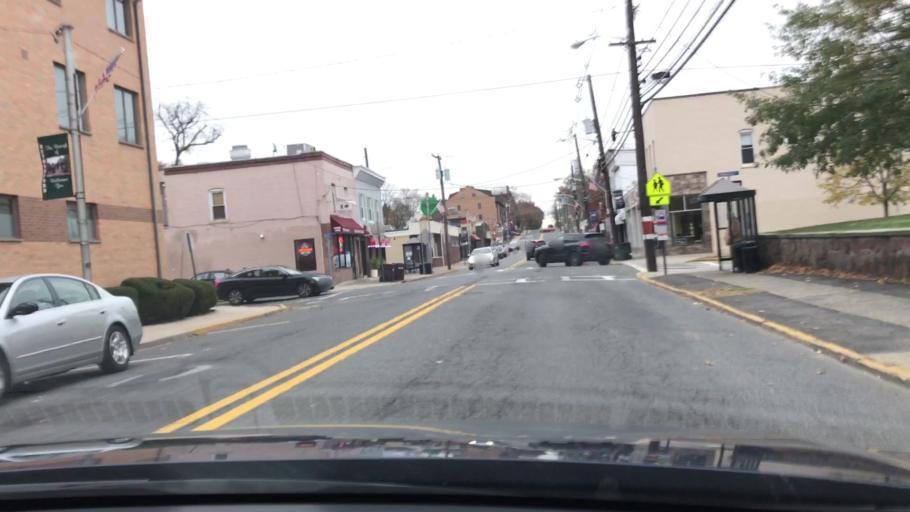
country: US
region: New Jersey
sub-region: Bergen County
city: Rutherford
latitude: 40.8368
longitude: -74.1146
